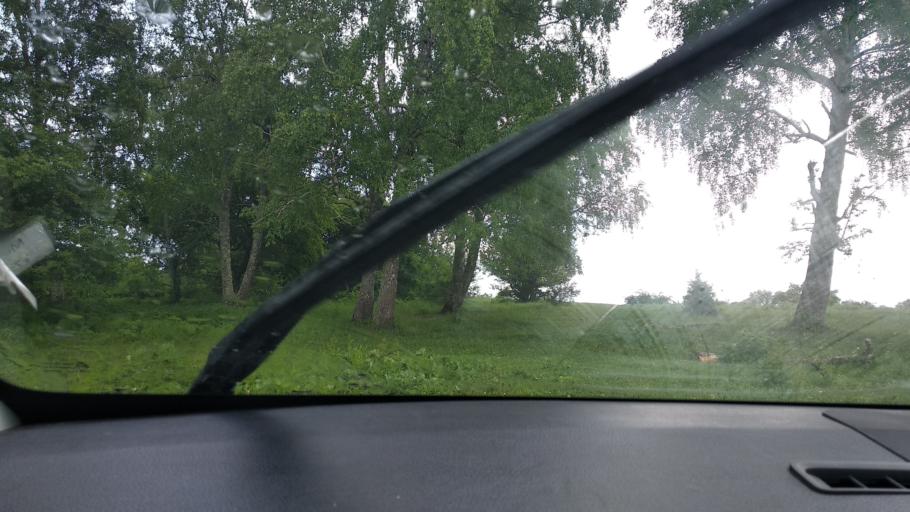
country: RU
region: Adygeya
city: Kamennomostskiy
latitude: 44.2227
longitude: 39.9971
